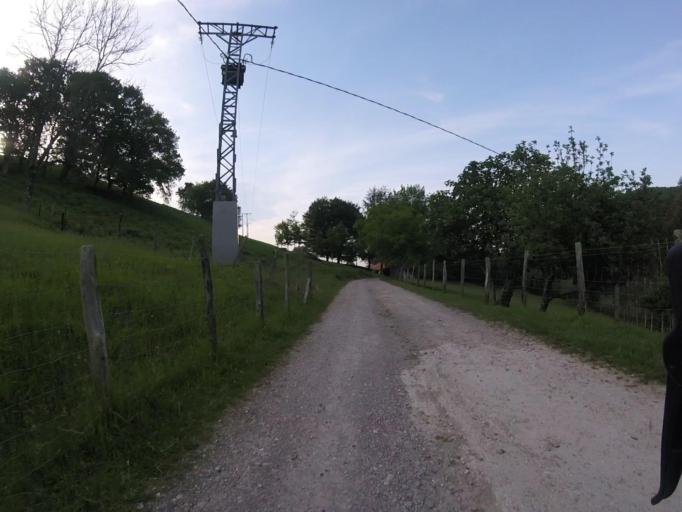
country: ES
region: Basque Country
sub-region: Provincia de Guipuzcoa
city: Errenteria
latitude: 43.2598
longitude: -1.8891
